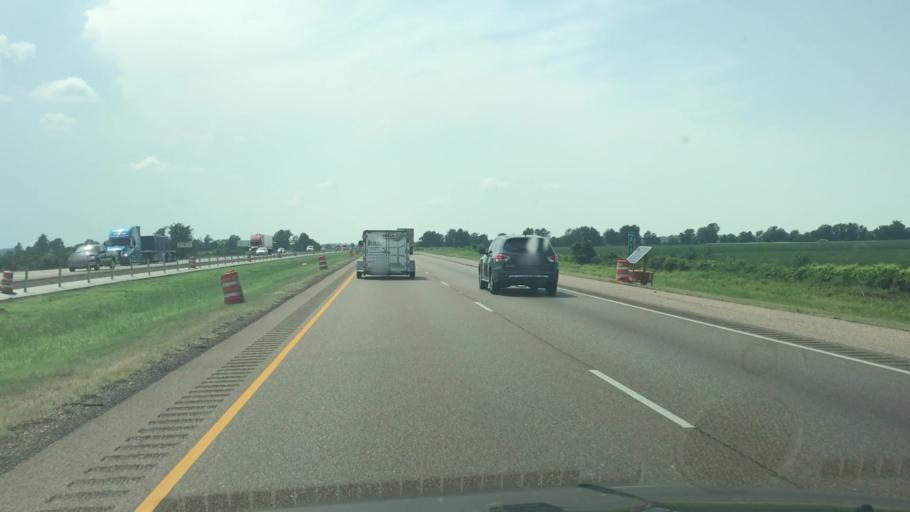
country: US
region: Arkansas
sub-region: Crittenden County
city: Earle
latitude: 35.1509
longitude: -90.3832
